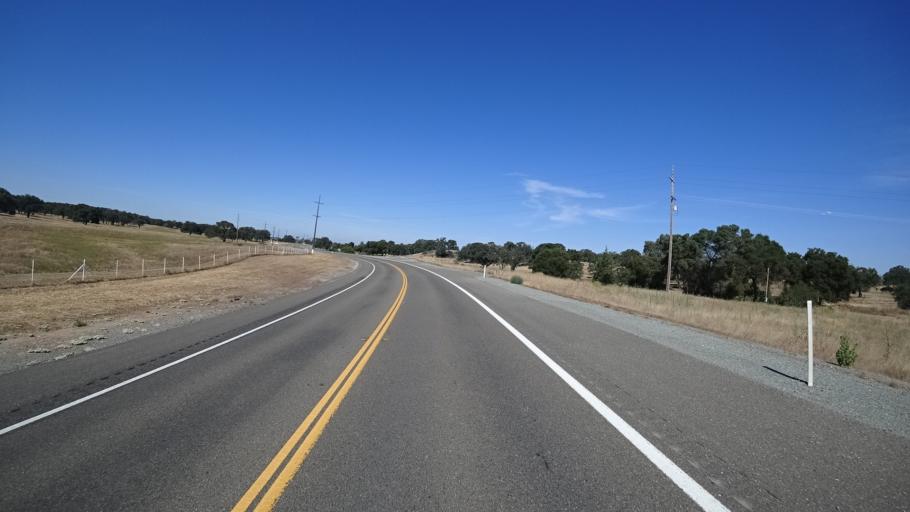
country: US
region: California
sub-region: Calaveras County
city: Rancho Calaveras
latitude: 38.1047
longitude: -120.9181
